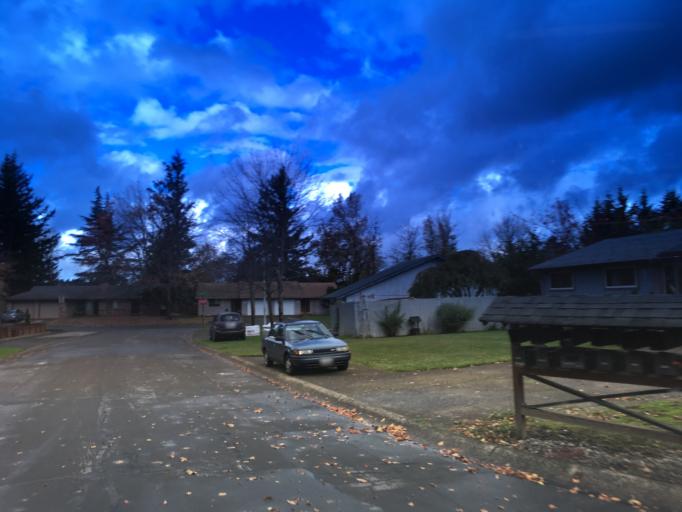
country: US
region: Oregon
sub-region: Multnomah County
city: Troutdale
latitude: 45.5155
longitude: -122.3855
